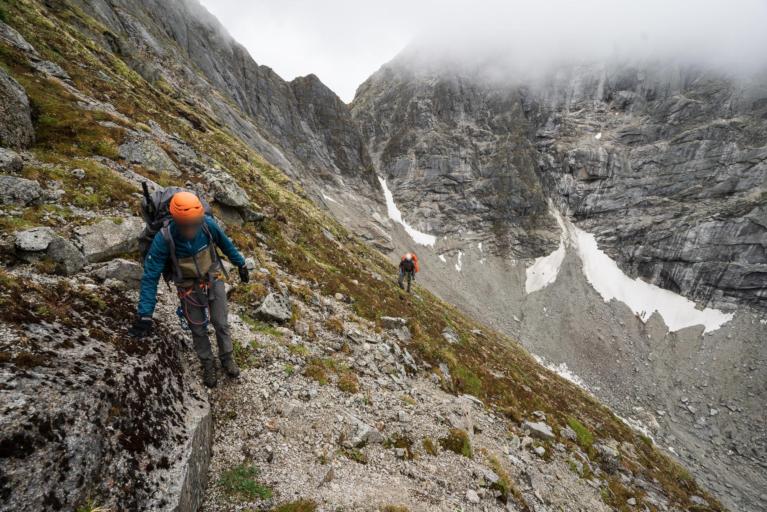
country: RU
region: Transbaikal Territory
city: Chara
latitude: 56.8679
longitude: 117.3854
